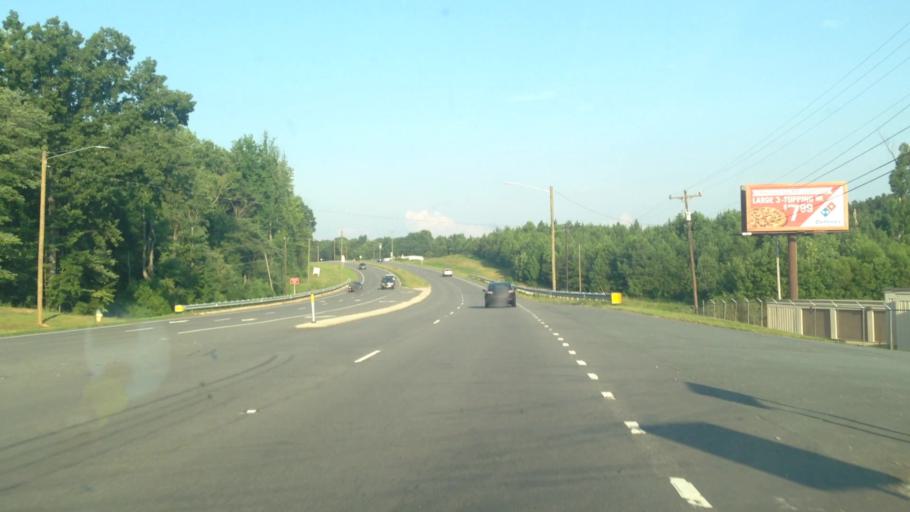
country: US
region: North Carolina
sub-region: Rockingham County
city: Reidsville
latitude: 36.3169
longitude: -79.6793
